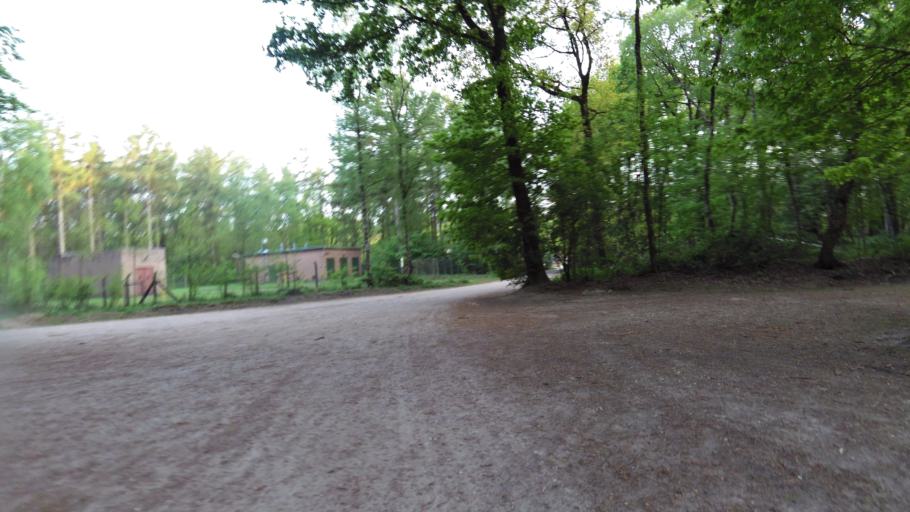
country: NL
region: Gelderland
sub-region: Gemeente Ede
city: Ede
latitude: 52.0262
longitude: 5.6866
